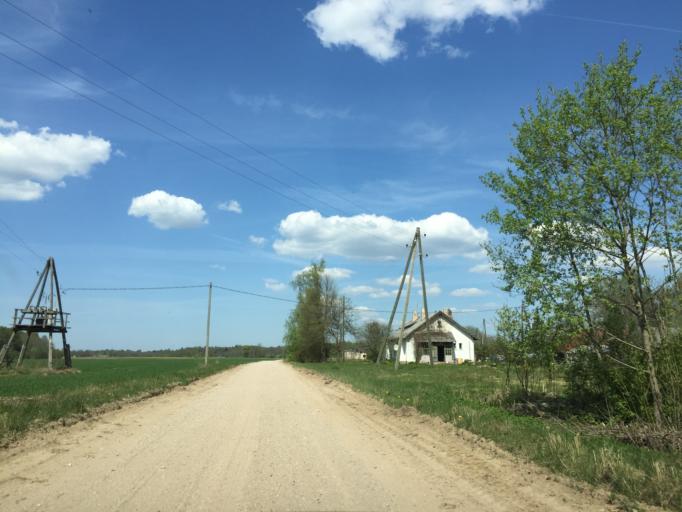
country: LV
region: Limbazu Rajons
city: Limbazi
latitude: 57.3697
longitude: 24.6345
